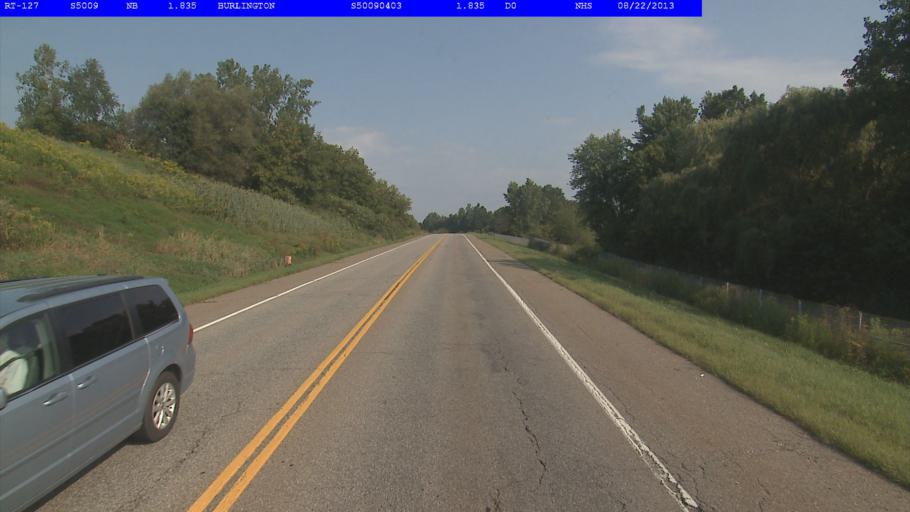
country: US
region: Vermont
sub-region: Chittenden County
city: Burlington
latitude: 44.5108
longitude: -73.2336
